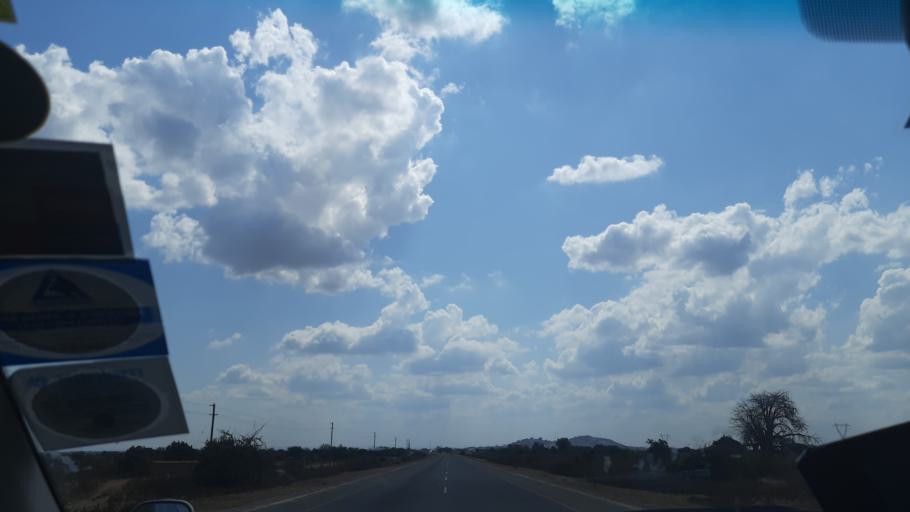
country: TZ
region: Singida
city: Kintinku
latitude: -5.9703
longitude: 35.3359
